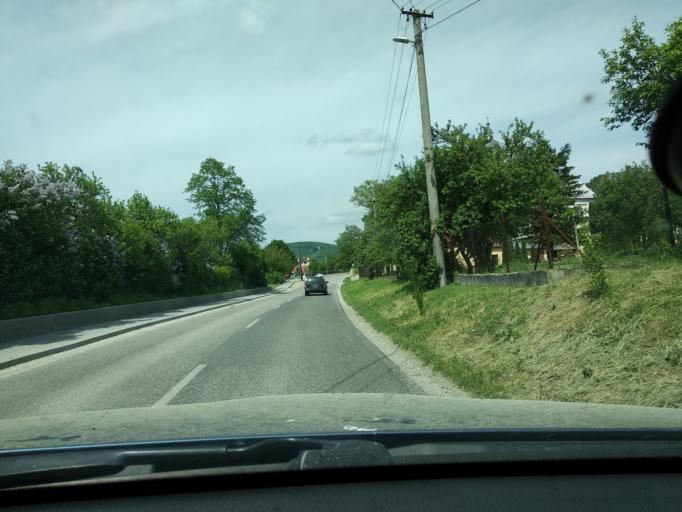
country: SK
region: Trenciansky
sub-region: Okres Nove Mesto nad Vahom
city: Nove Mesto nad Vahom
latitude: 48.8224
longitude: 17.8437
